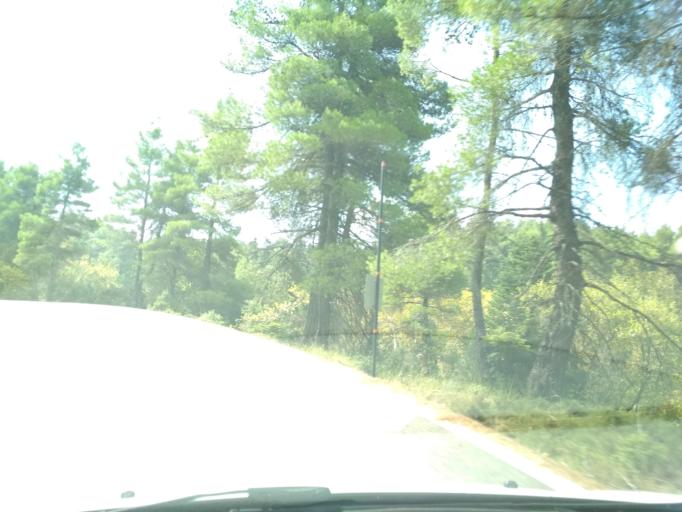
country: GR
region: Central Greece
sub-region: Nomos Evvoias
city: Politika
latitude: 38.6593
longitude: 23.5561
